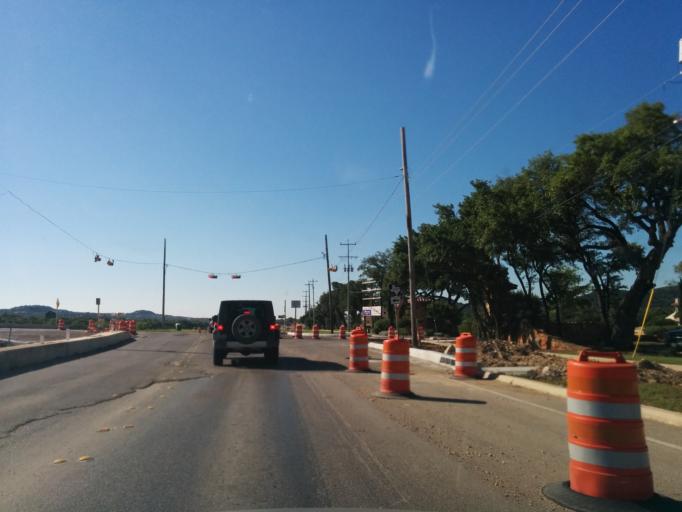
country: US
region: Texas
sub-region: Bexar County
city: Cross Mountain
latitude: 29.6763
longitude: -98.6370
